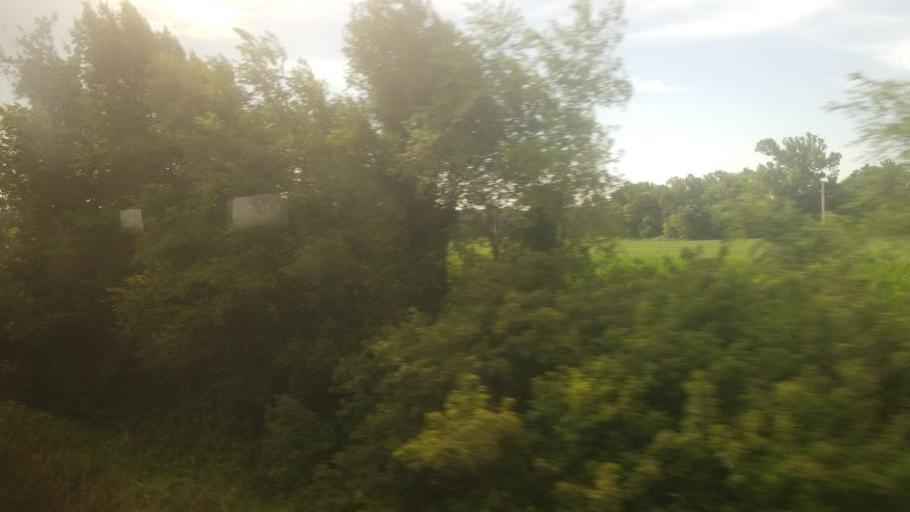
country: US
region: Kansas
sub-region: Douglas County
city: Eudora
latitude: 38.9648
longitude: -95.0604
